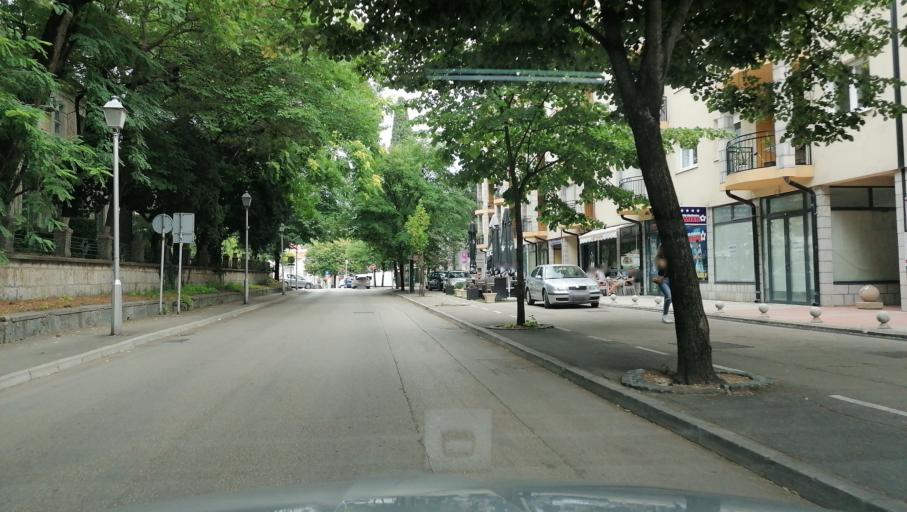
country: BA
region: Republika Srpska
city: Trebinje
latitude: 42.7125
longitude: 18.3411
